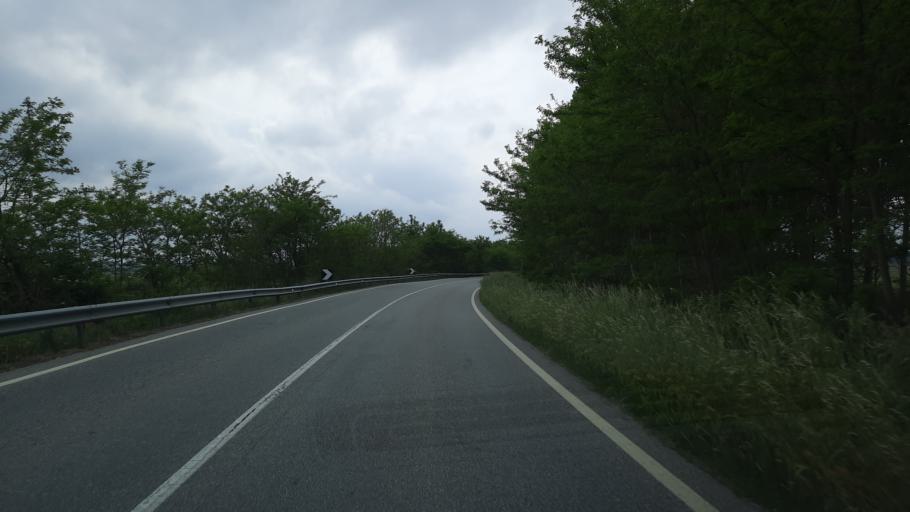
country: IT
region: Piedmont
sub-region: Provincia di Vercelli
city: Motta De Conti
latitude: 45.2052
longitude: 8.5391
